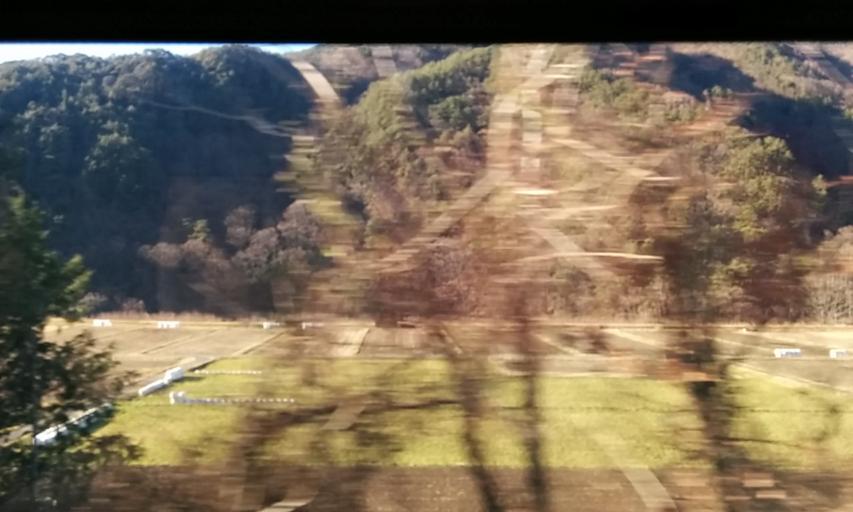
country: JP
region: Nagano
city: Ina
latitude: 35.8818
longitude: 137.7562
